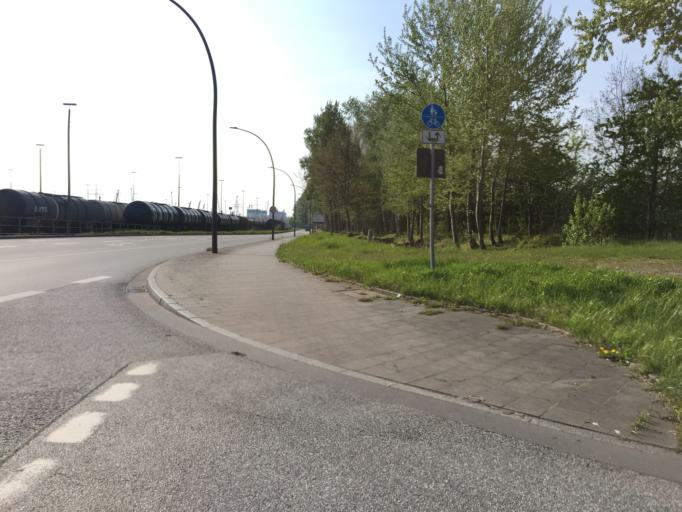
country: DE
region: Hamburg
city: Kleiner Grasbrook
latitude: 53.4991
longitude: 9.9696
